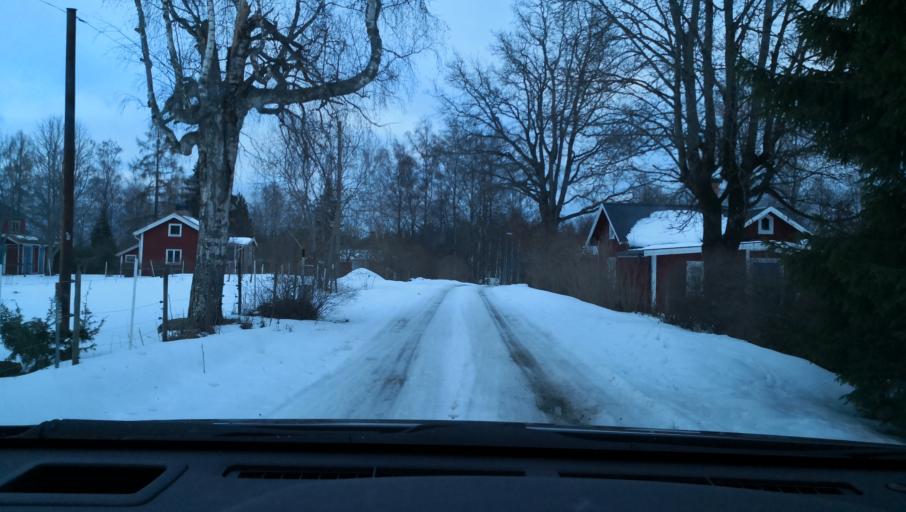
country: SE
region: Dalarna
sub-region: Smedjebackens Kommun
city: Smedjebacken
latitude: 60.0625
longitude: 15.5560
